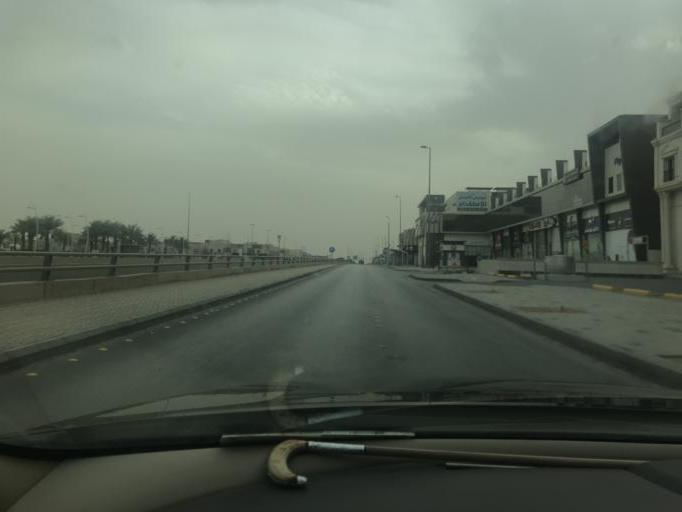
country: SA
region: Ar Riyad
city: Riyadh
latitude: 24.7698
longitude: 46.7150
